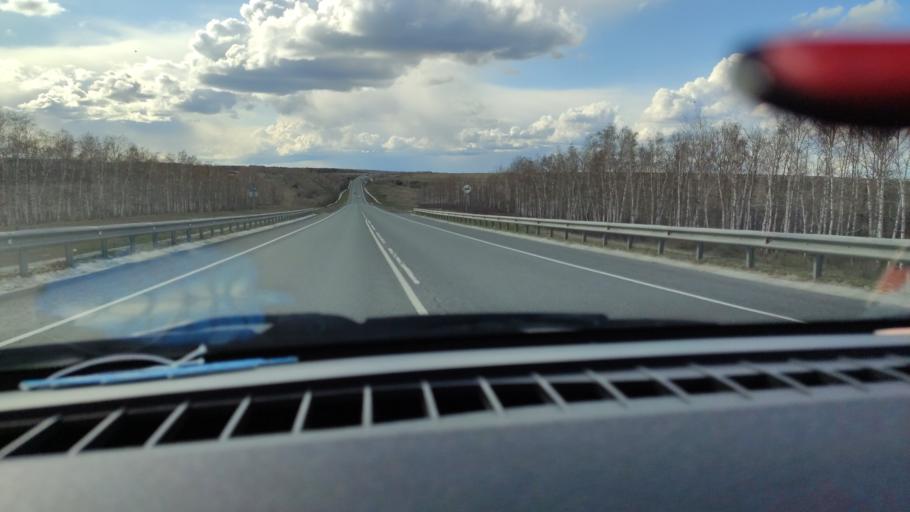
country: RU
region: Saratov
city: Shikhany
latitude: 52.1259
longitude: 47.2437
